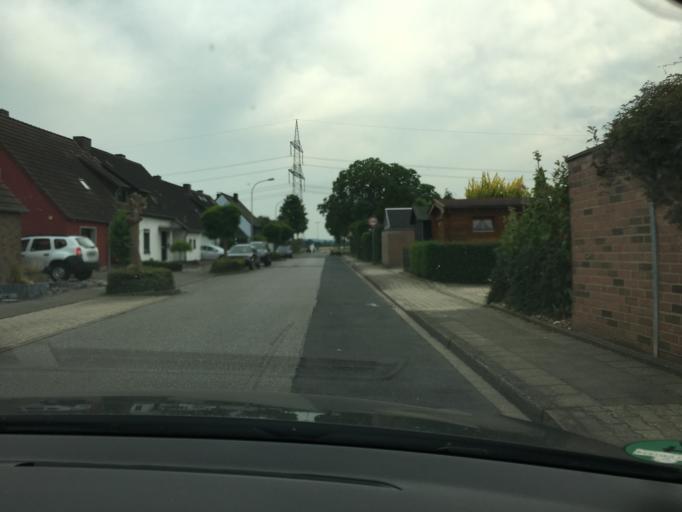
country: DE
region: North Rhine-Westphalia
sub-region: Regierungsbezirk Koln
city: Merzenich
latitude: 50.8247
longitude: 6.5182
